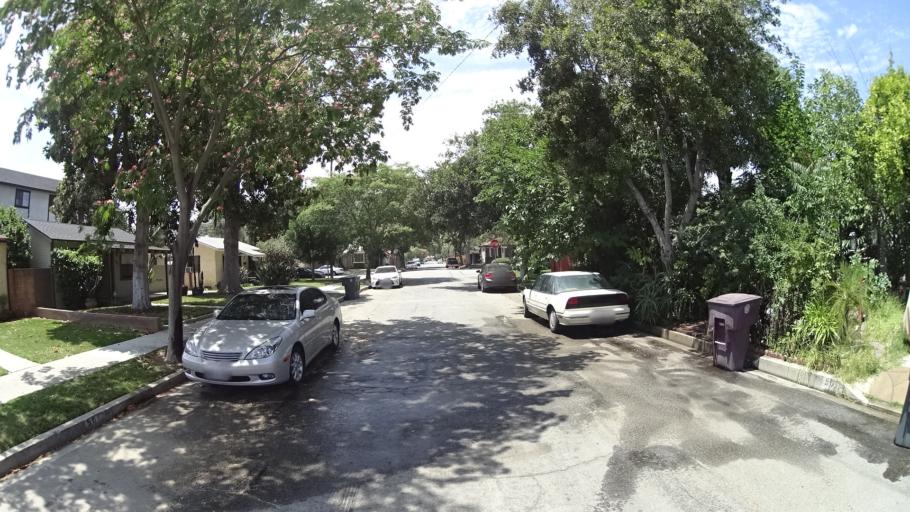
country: US
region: California
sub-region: Los Angeles County
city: Burbank
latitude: 34.1617
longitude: -118.2946
